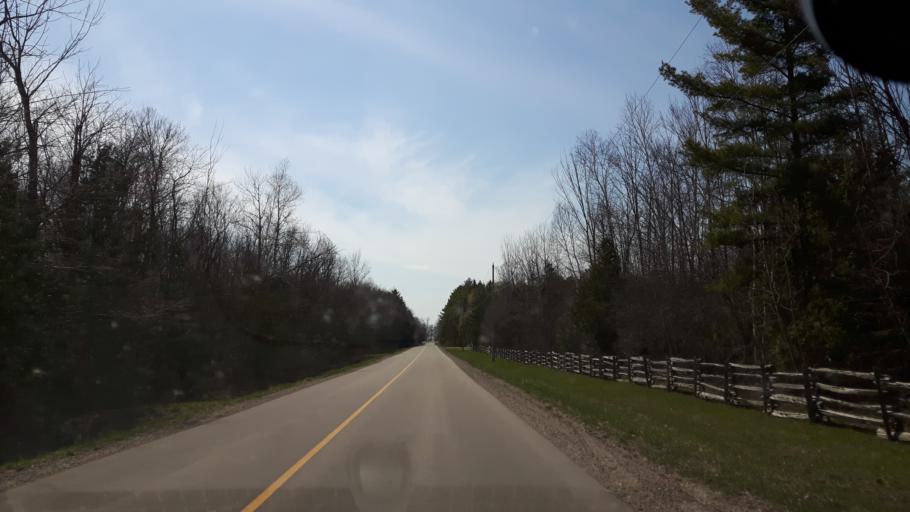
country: CA
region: Ontario
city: Bluewater
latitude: 43.5758
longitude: -81.6976
